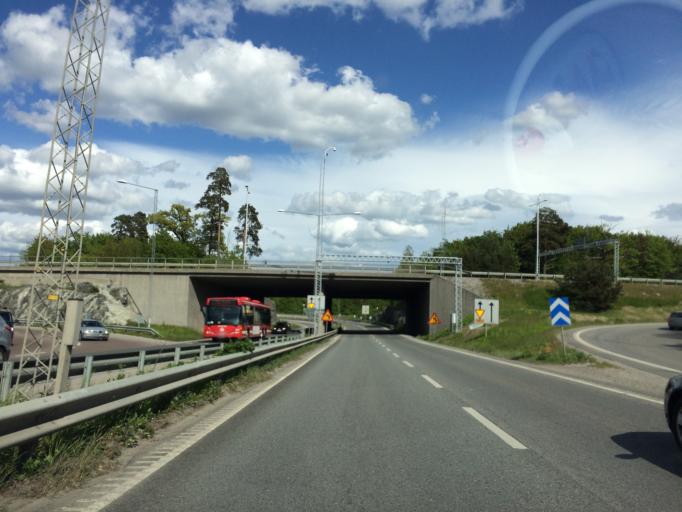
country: SE
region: Stockholm
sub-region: Norrtalje Kommun
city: Bergshamra
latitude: 59.3800
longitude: 18.0403
